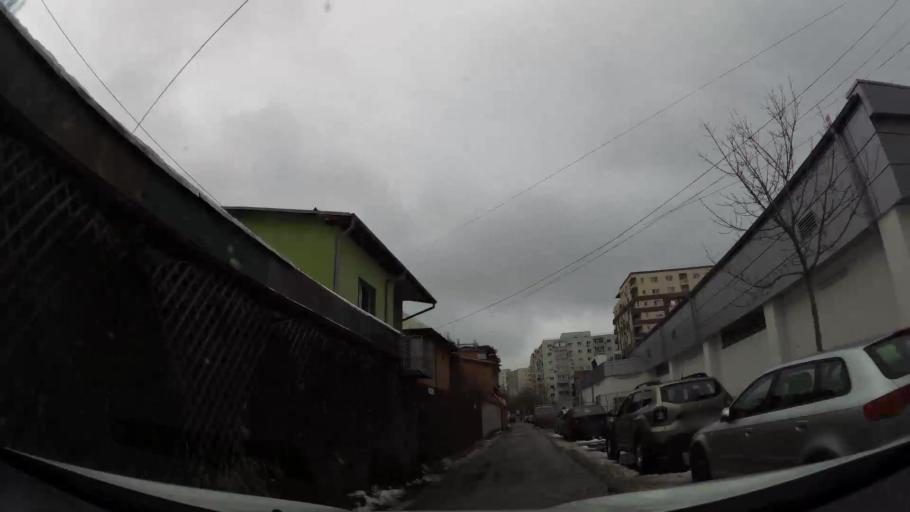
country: RO
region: Bucuresti
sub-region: Municipiul Bucuresti
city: Bucharest
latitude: 44.4156
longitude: 26.1394
